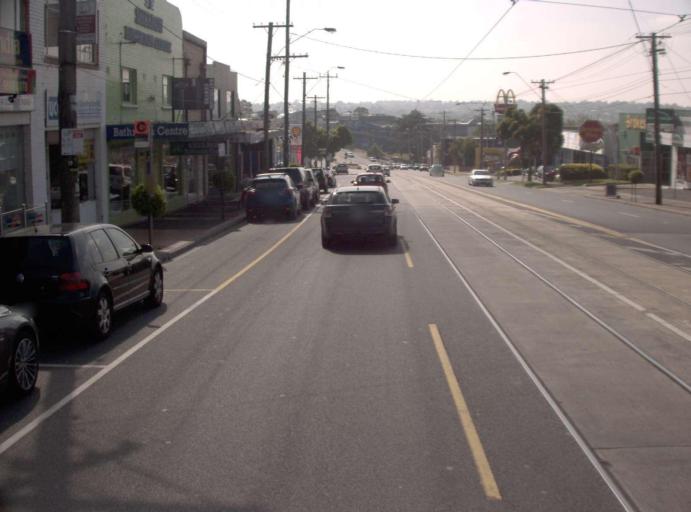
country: AU
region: Victoria
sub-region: Monash
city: Ashwood
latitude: -37.8504
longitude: 145.0962
